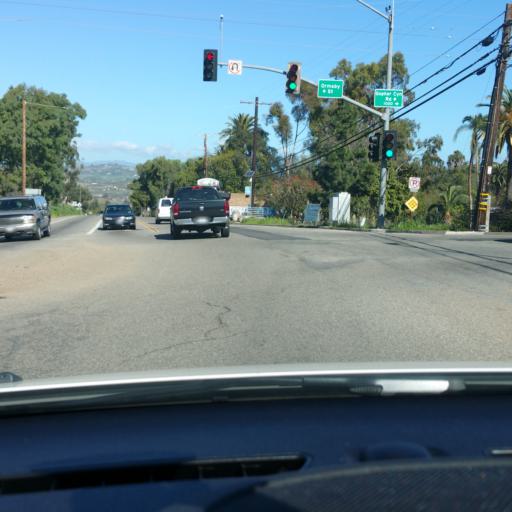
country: US
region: California
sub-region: San Diego County
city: Bonsall
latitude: 33.2469
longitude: -117.2278
